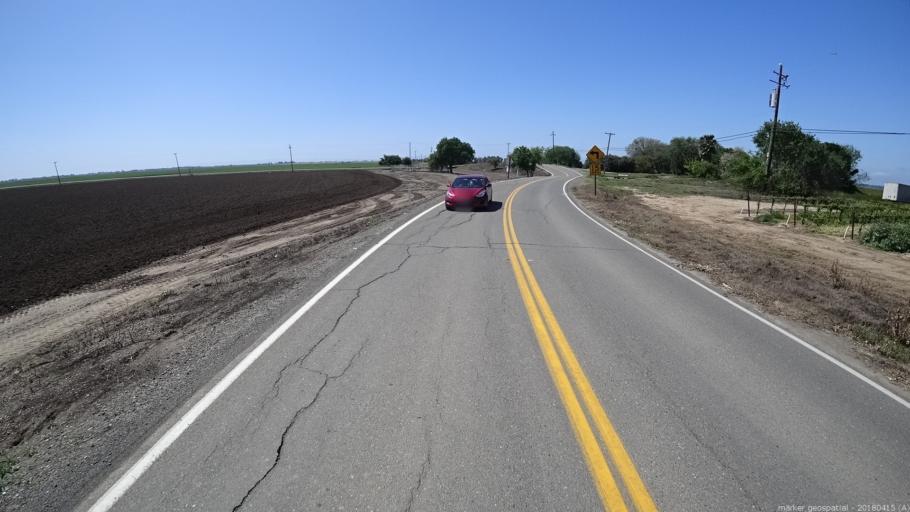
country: US
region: California
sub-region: Solano County
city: Rio Vista
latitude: 38.1504
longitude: -121.6146
